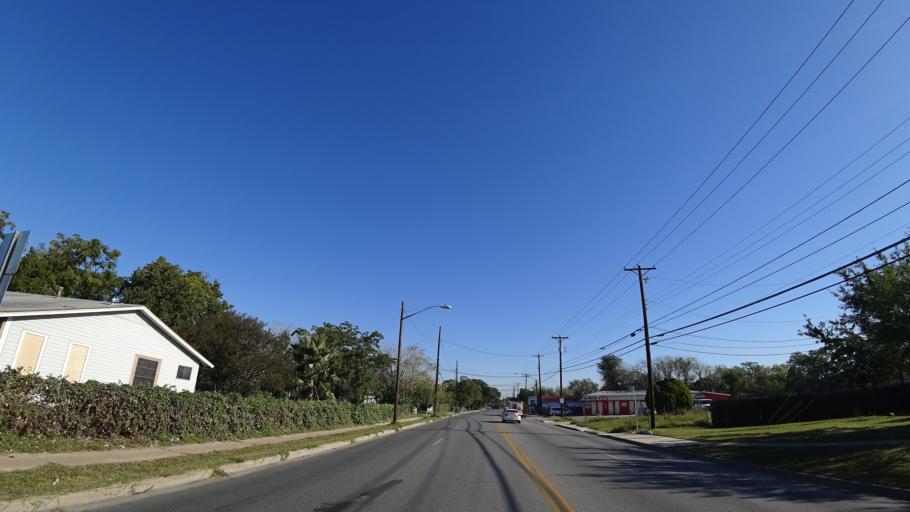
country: US
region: Texas
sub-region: Travis County
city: Austin
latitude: 30.2346
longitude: -97.6973
